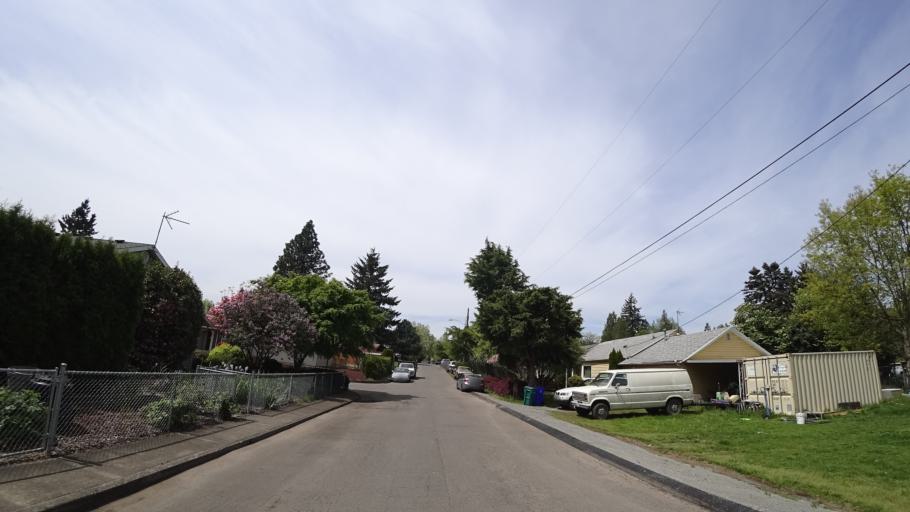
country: US
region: Oregon
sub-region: Clackamas County
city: Milwaukie
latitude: 45.4499
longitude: -122.6160
